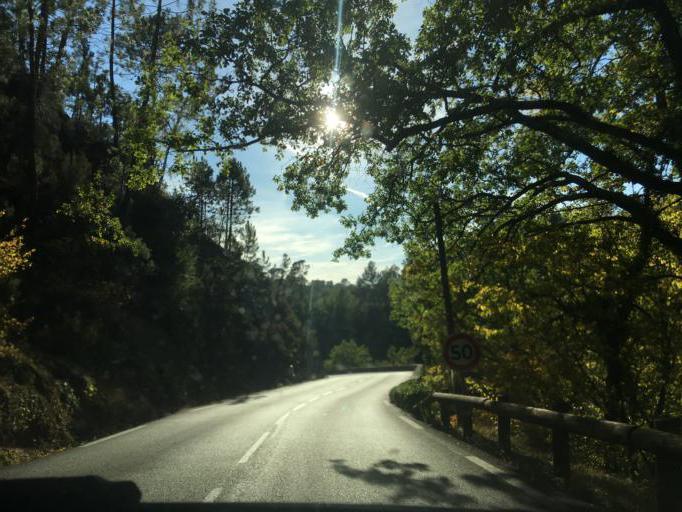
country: FR
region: Provence-Alpes-Cote d'Azur
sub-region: Departement du Var
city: Callas
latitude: 43.5509
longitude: 6.5733
